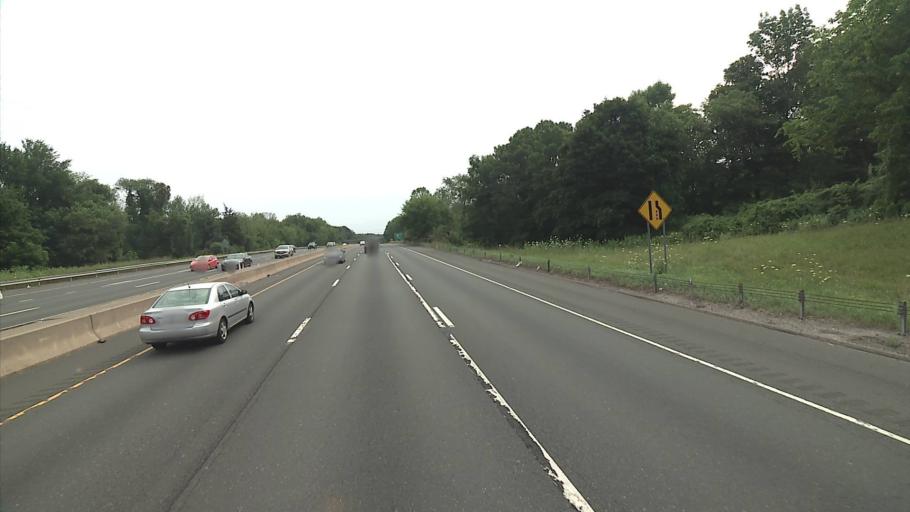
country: US
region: Connecticut
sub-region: Fairfield County
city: Bethel
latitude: 41.4205
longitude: -73.3897
